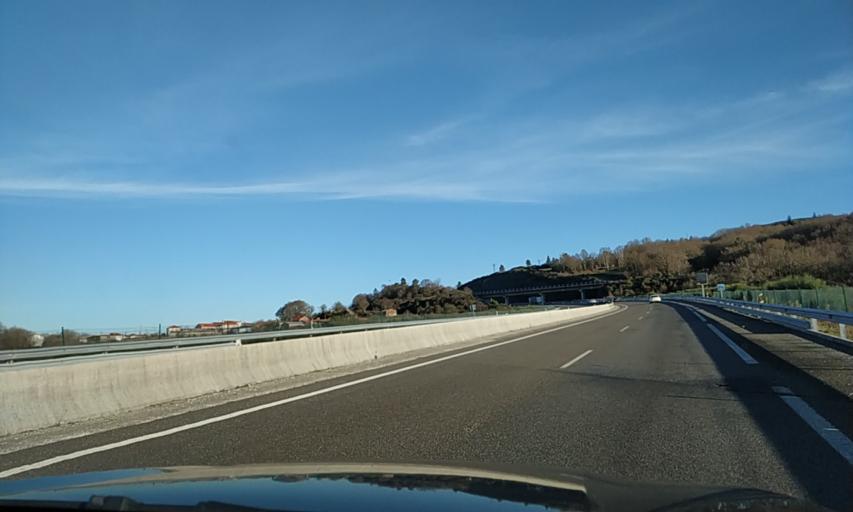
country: ES
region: Galicia
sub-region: Provincia de Pontevedra
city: Dozon
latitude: 42.5674
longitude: -8.0545
